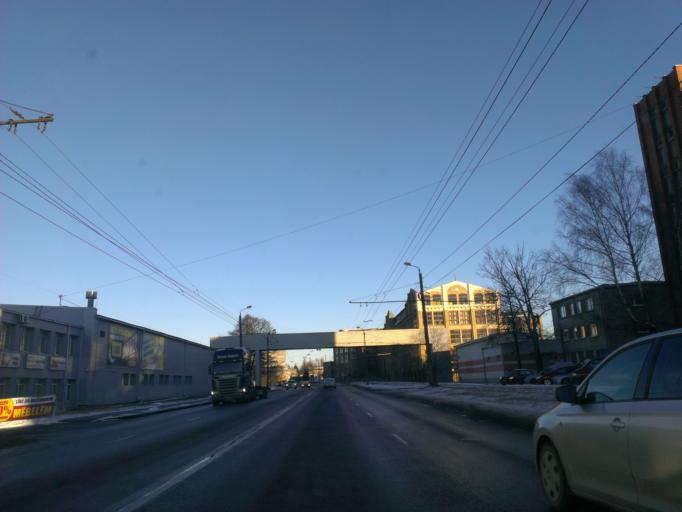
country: LV
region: Riga
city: Riga
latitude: 56.9845
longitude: 24.1198
